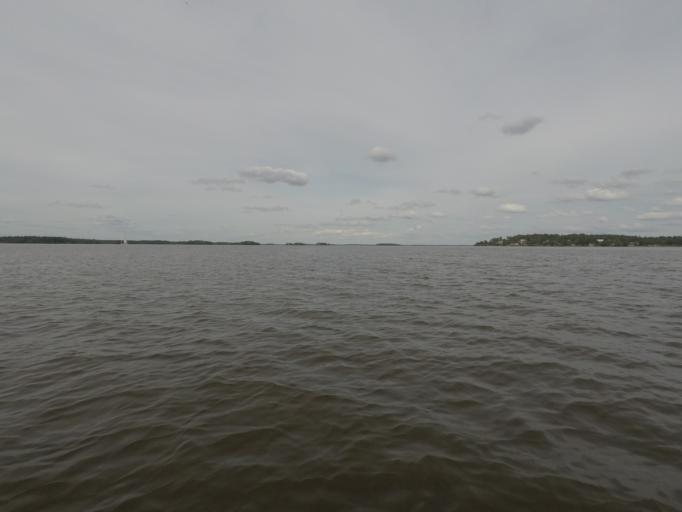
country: SE
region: Soedermanland
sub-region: Eskilstuna Kommun
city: Torshalla
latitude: 59.4580
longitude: 16.4318
